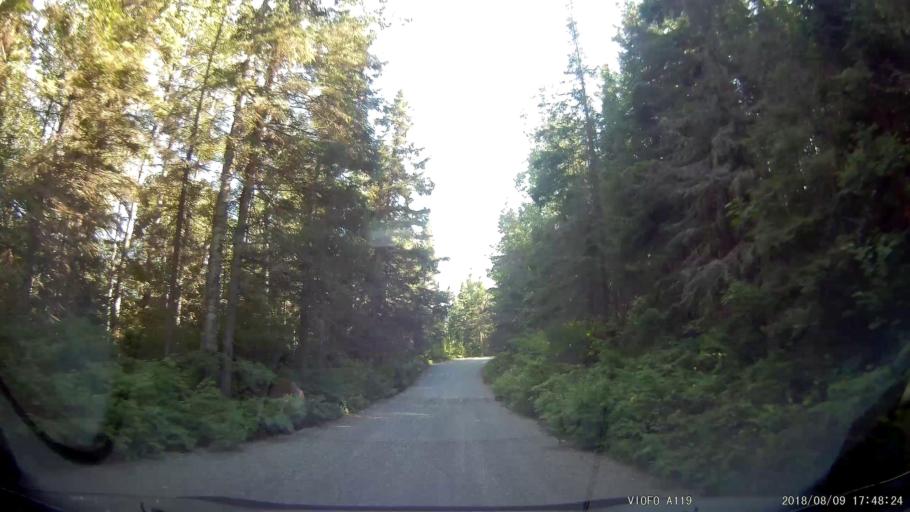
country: CA
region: Ontario
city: Rayside-Balfour
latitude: 46.5902
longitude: -81.5402
